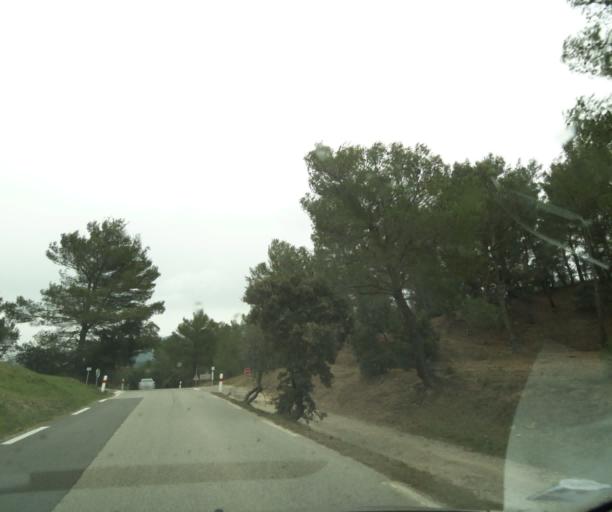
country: FR
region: Provence-Alpes-Cote d'Azur
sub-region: Departement des Bouches-du-Rhone
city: Saint-Marc-Jaumegarde
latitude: 43.5546
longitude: 5.5769
